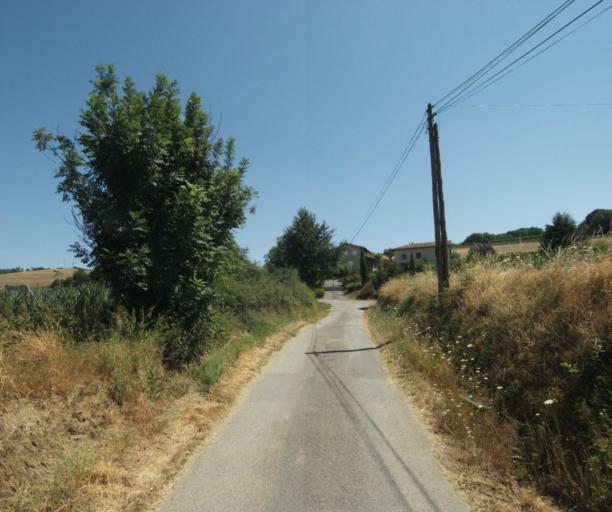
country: FR
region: Rhone-Alpes
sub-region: Departement du Rhone
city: Courzieu
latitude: 45.7496
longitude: 4.5540
